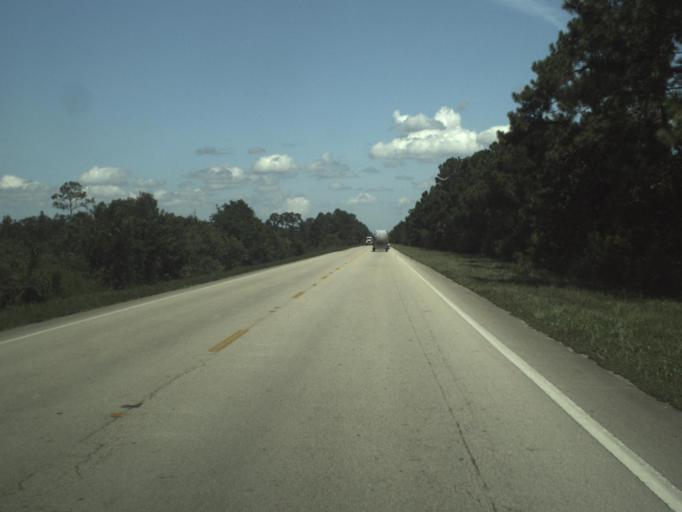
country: US
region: Florida
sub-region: Martin County
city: Indiantown
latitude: 26.9787
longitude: -80.4050
